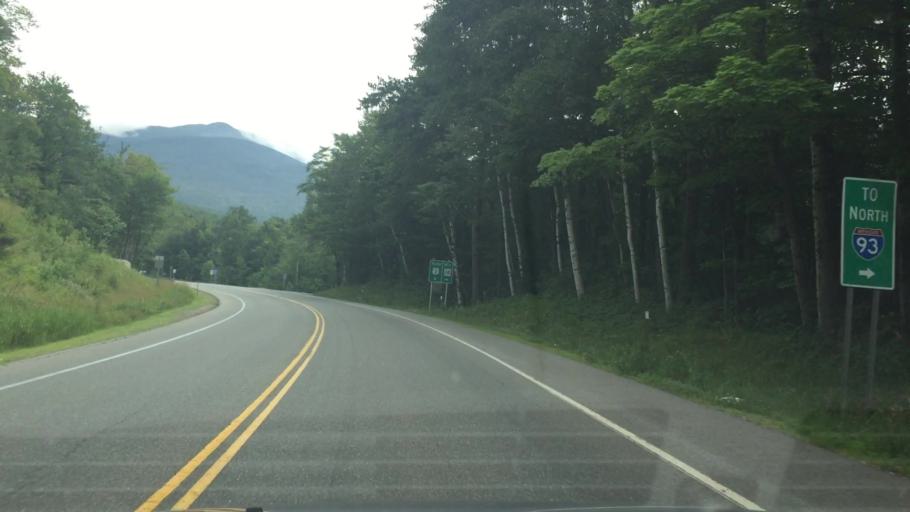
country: US
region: New Hampshire
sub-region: Grafton County
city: Deerfield
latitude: 44.2079
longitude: -71.6847
